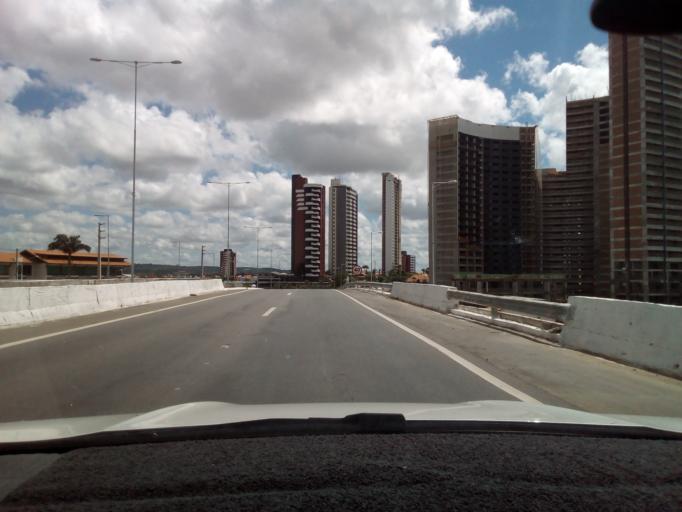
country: BR
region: Paraiba
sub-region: Campina Grande
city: Campina Grande
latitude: -7.2393
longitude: -35.8690
